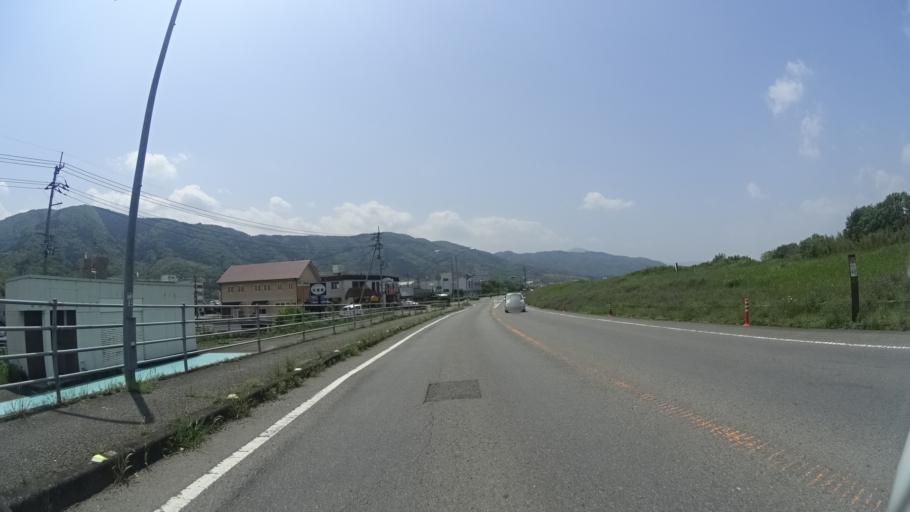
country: JP
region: Tokushima
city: Kamojimacho-jogejima
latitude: 34.0625
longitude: 134.3163
